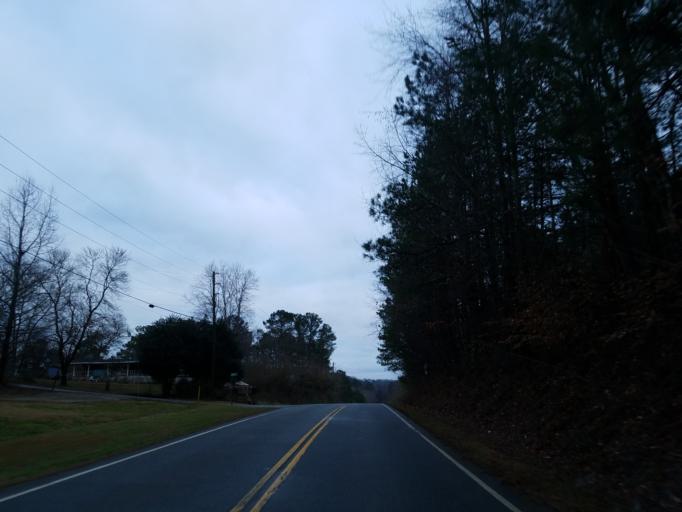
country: US
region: Georgia
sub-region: Bartow County
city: Emerson
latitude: 34.0994
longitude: -84.7357
